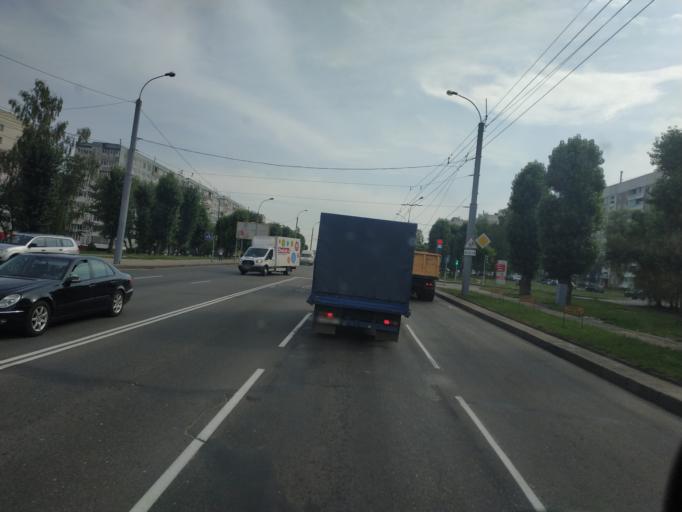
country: BY
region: Mogilev
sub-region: Mahilyowski Rayon
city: Veyno
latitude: 53.8751
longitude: 30.3772
